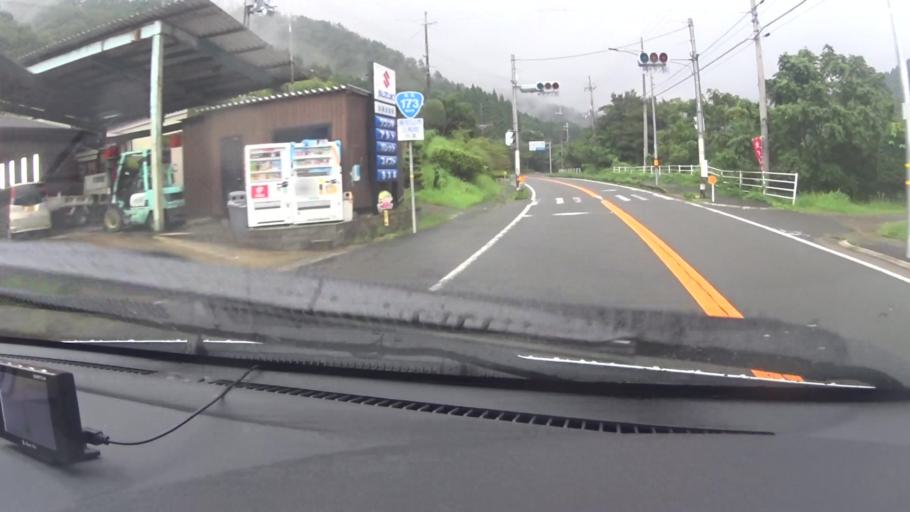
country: JP
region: Kyoto
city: Ayabe
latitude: 35.2494
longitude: 135.2778
